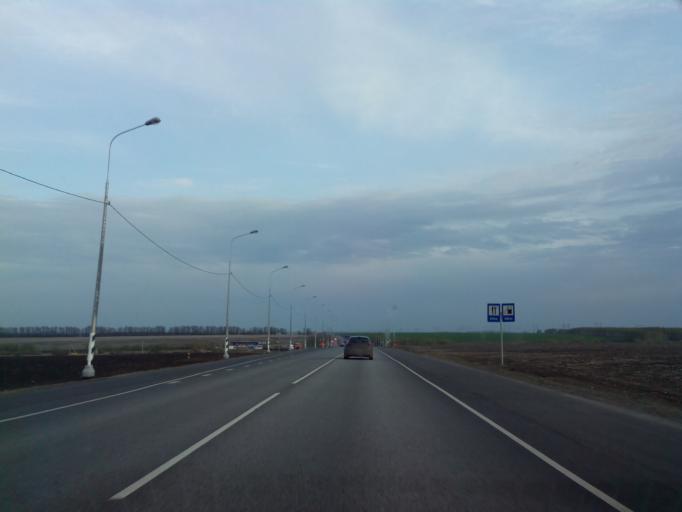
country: RU
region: Rjazan
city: Ryazhsk
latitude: 53.5611
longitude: 40.0513
